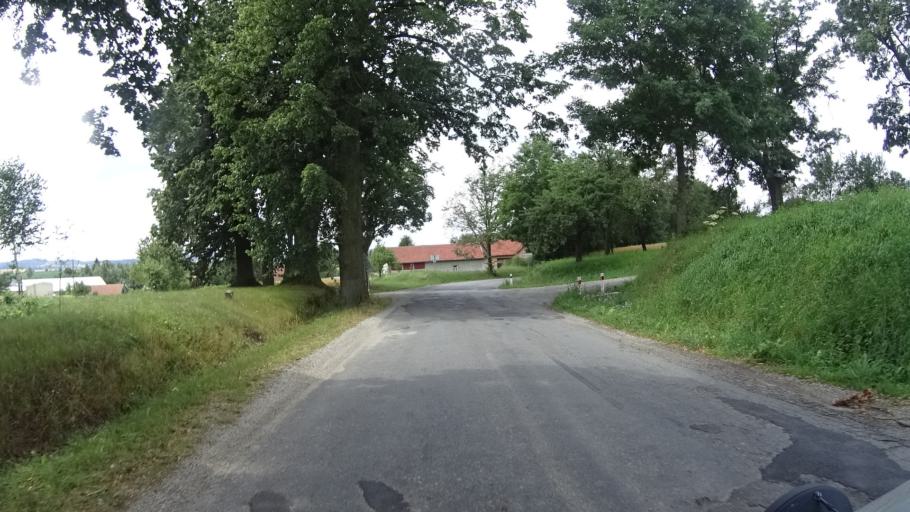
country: CZ
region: Vysocina
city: Merin
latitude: 49.4014
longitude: 15.9130
